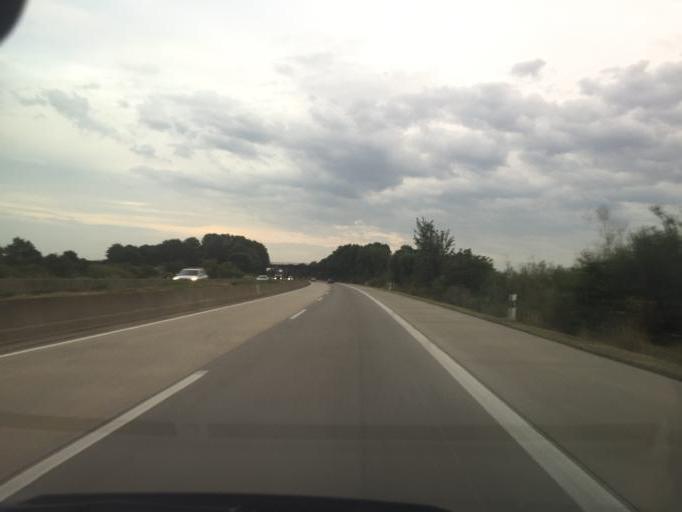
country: DE
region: North Rhine-Westphalia
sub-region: Regierungsbezirk Koln
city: Titz
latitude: 51.0175
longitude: 6.4893
